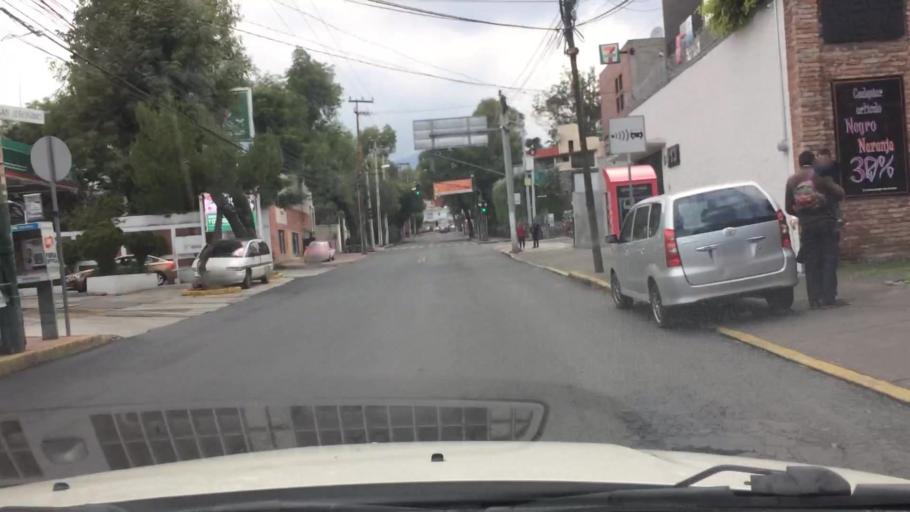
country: MX
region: Mexico City
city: Magdalena Contreras
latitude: 19.3284
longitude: -99.2181
